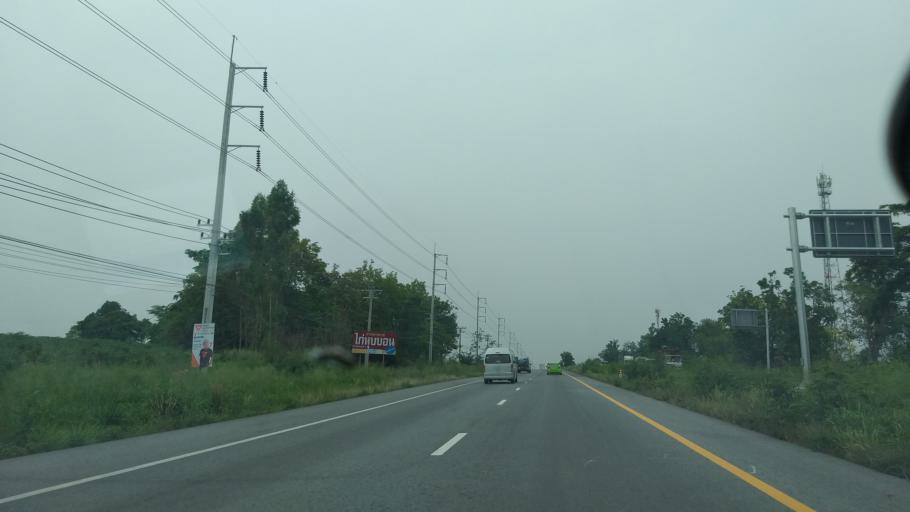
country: TH
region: Chon Buri
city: Ko Chan
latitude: 13.4298
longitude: 101.2828
